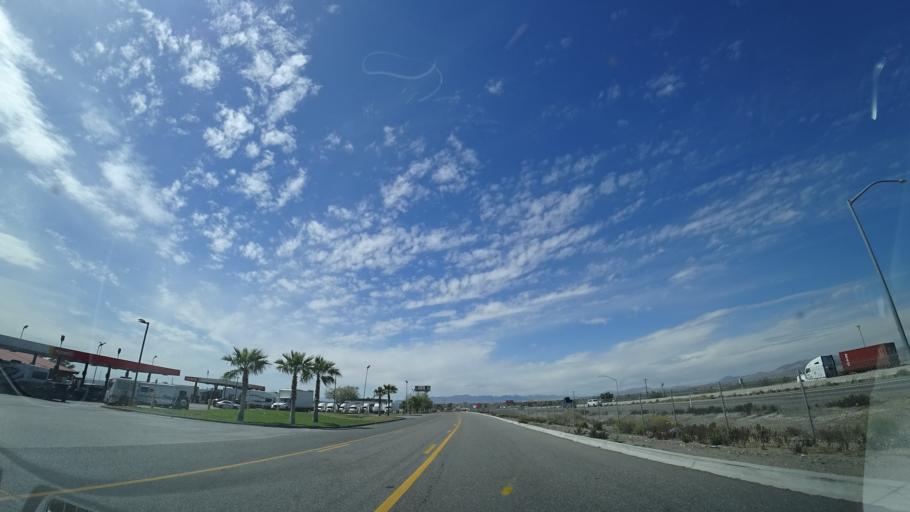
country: US
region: Arizona
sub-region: La Paz County
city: Ehrenberg
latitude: 33.6024
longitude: -114.5222
